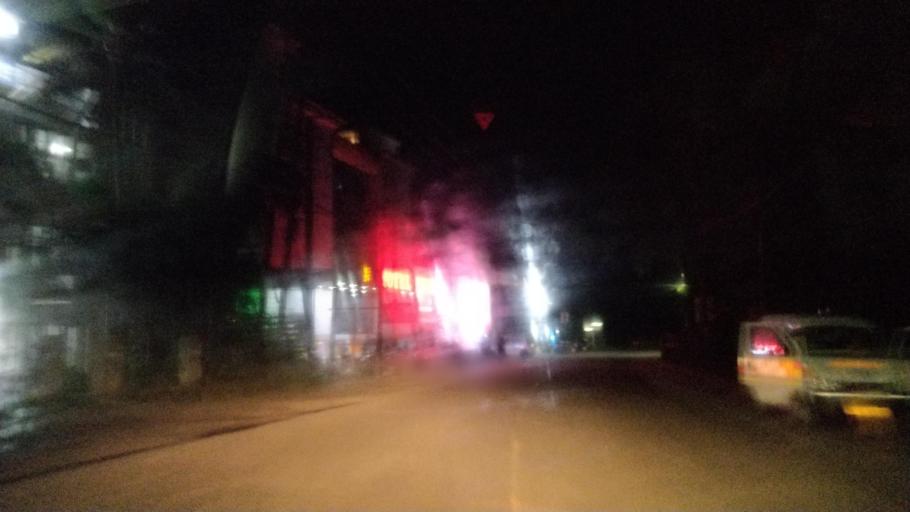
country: IN
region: Kerala
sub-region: Kottayam
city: Kottayam
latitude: 9.6306
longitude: 76.5261
